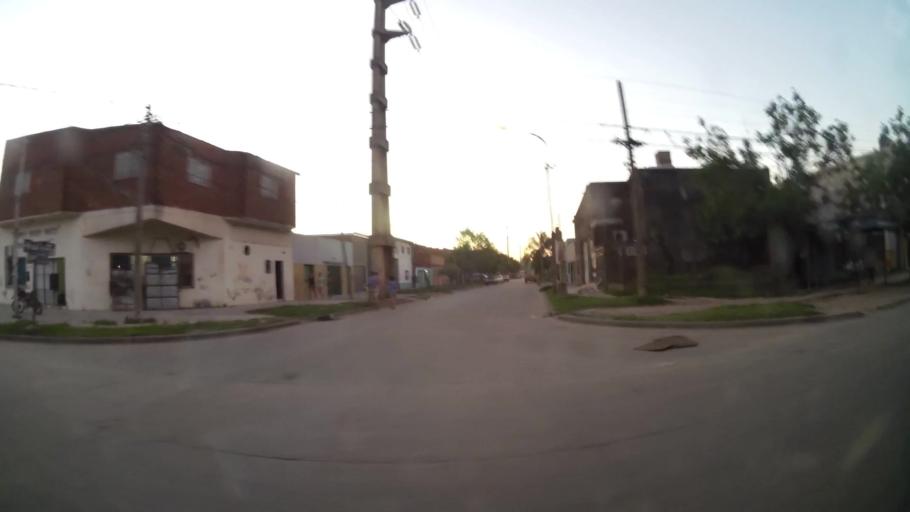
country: AR
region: Santa Fe
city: Santa Fe de la Vera Cruz
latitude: -31.6083
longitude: -60.7130
